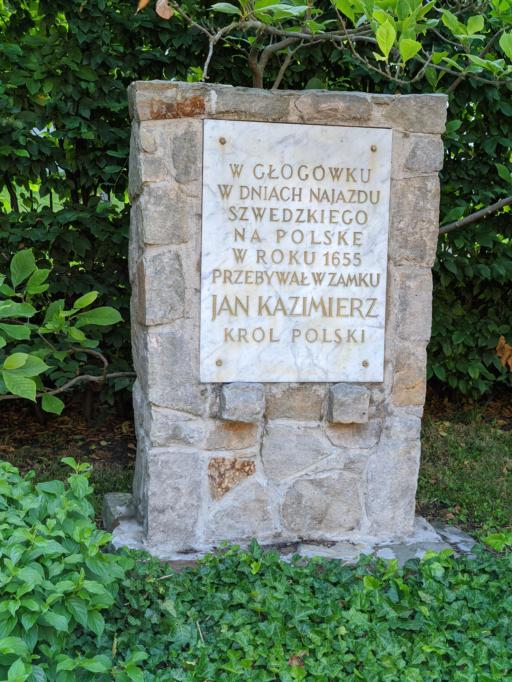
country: PL
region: Opole Voivodeship
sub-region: Powiat prudnicki
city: Glogowek
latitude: 50.3552
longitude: 17.8618
